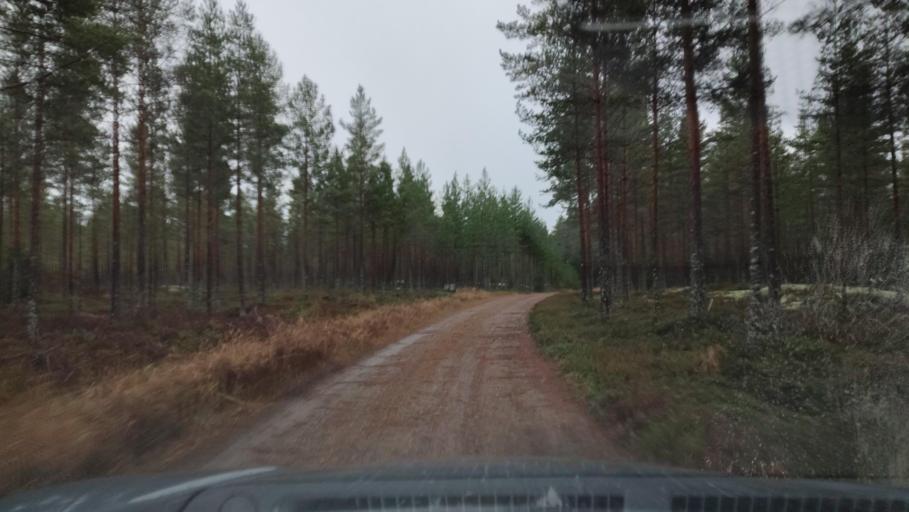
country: FI
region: Southern Ostrobothnia
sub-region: Suupohja
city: Karijoki
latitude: 62.1545
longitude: 21.5901
